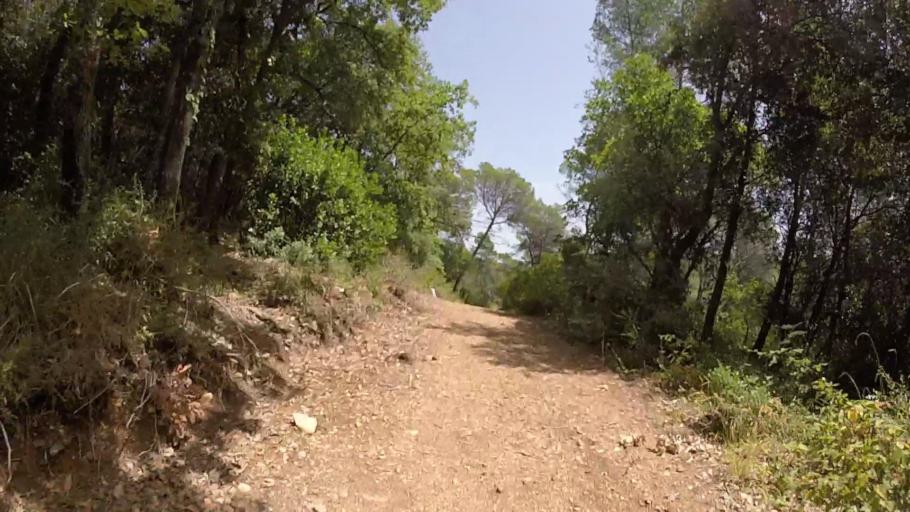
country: FR
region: Provence-Alpes-Cote d'Azur
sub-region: Departement des Alpes-Maritimes
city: Valbonne
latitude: 43.6205
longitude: 7.0145
